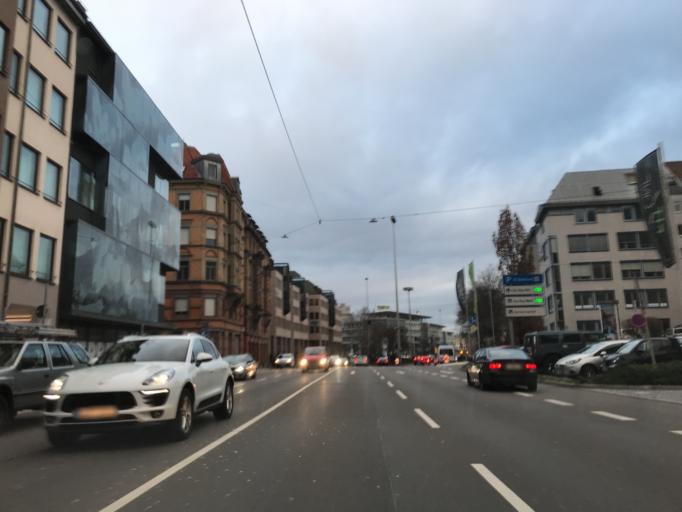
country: DE
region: Baden-Wuerttemberg
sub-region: Regierungsbezirk Stuttgart
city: Stuttgart
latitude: 48.7658
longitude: 9.1720
